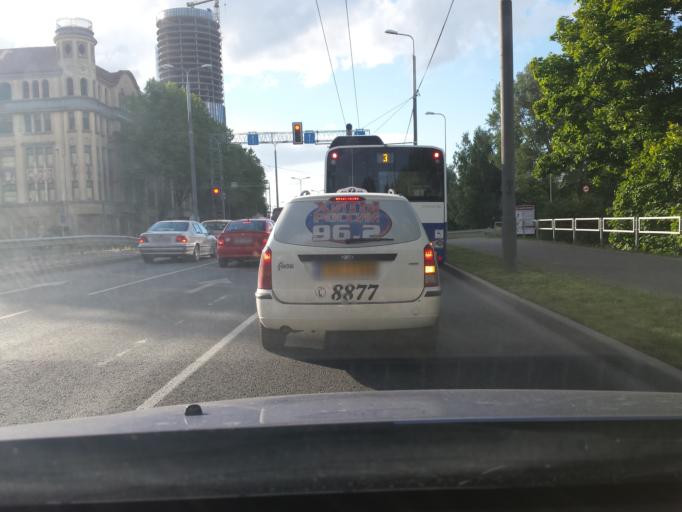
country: LV
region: Riga
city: Riga
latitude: 56.9444
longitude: 24.0847
